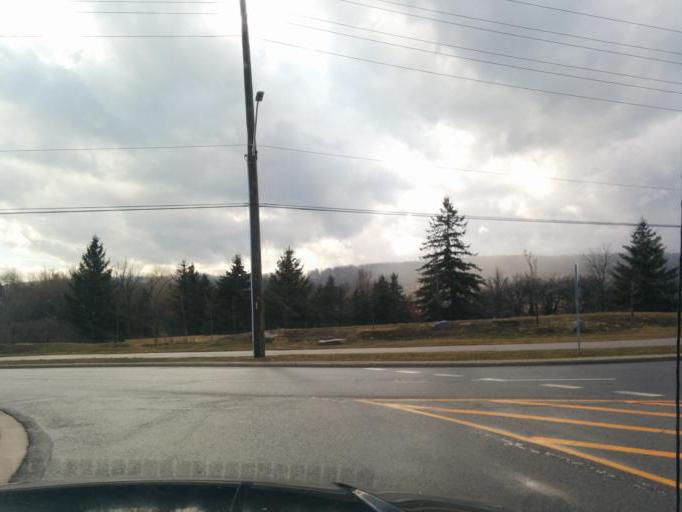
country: CA
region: Ontario
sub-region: Halton
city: Milton
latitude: 43.4956
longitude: -79.8974
